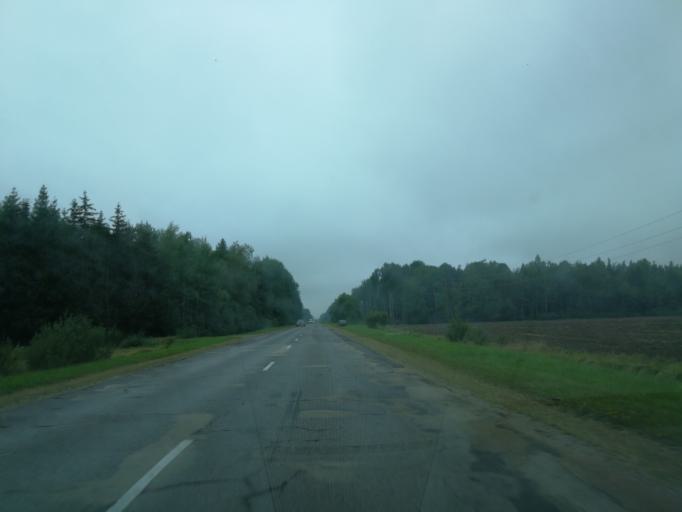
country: LV
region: Varkava
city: Vecvarkava
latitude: 56.3198
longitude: 26.4440
